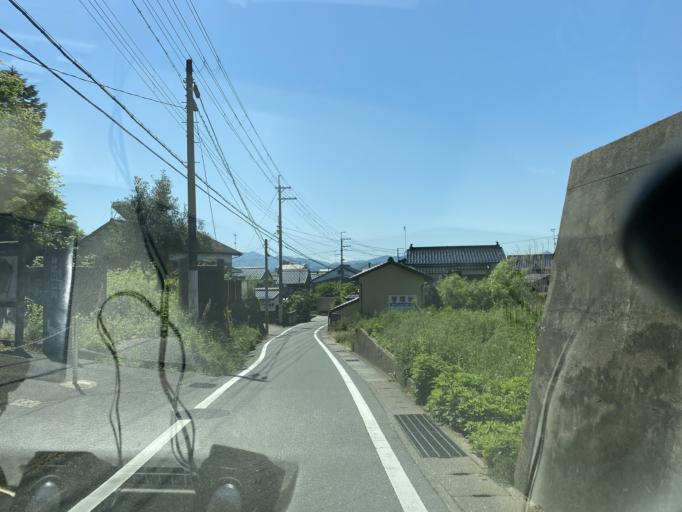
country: JP
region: Hyogo
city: Toyooka
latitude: 35.5394
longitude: 134.8194
